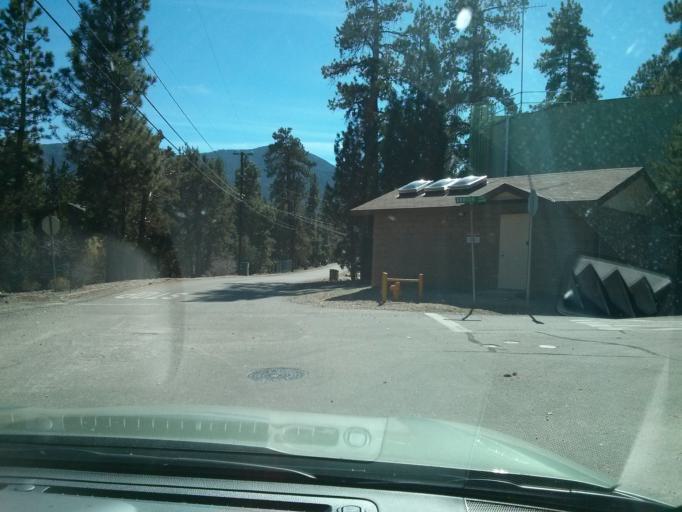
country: US
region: California
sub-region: San Bernardino County
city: Big Bear City
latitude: 34.2433
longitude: -116.8229
